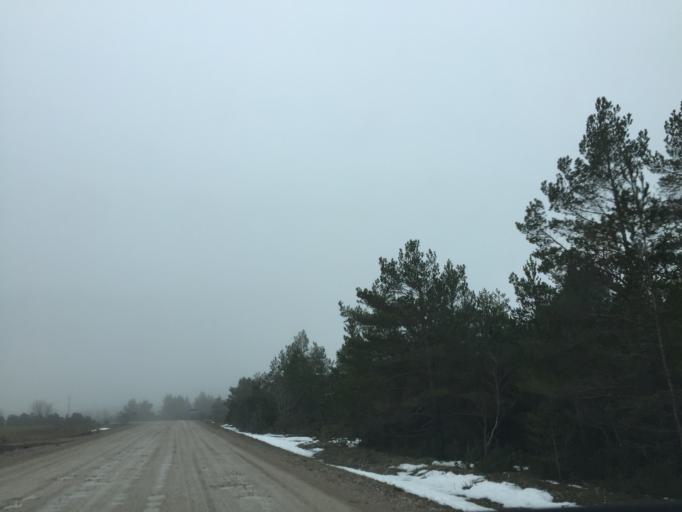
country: EE
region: Saare
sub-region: Kuressaare linn
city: Kuressaare
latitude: 58.4697
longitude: 22.0015
